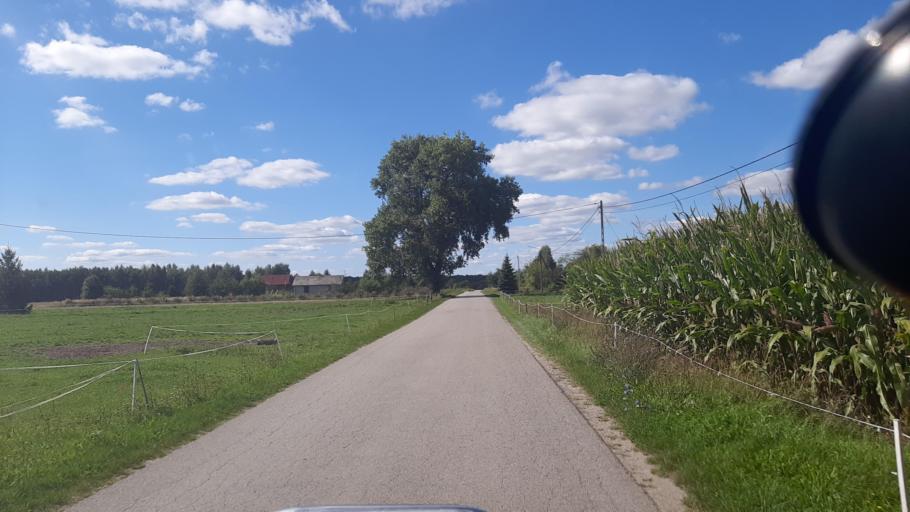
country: PL
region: Lublin Voivodeship
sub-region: Powiat lubelski
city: Garbow
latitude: 51.4070
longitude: 22.3990
